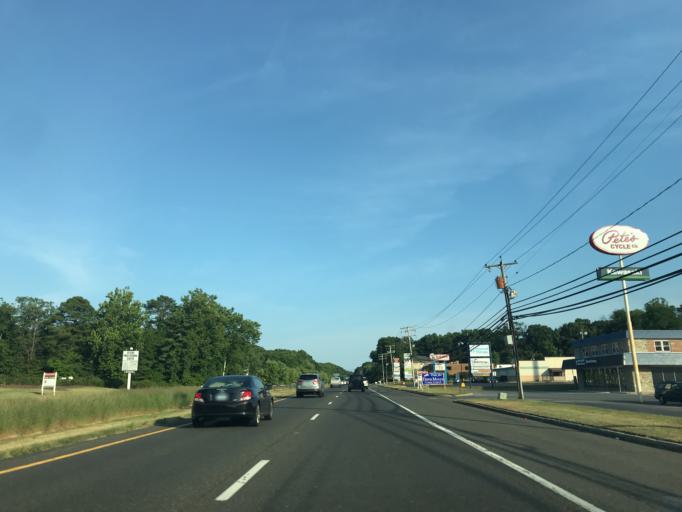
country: US
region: Maryland
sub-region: Anne Arundel County
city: Severna Park
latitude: 39.0663
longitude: -76.5359
